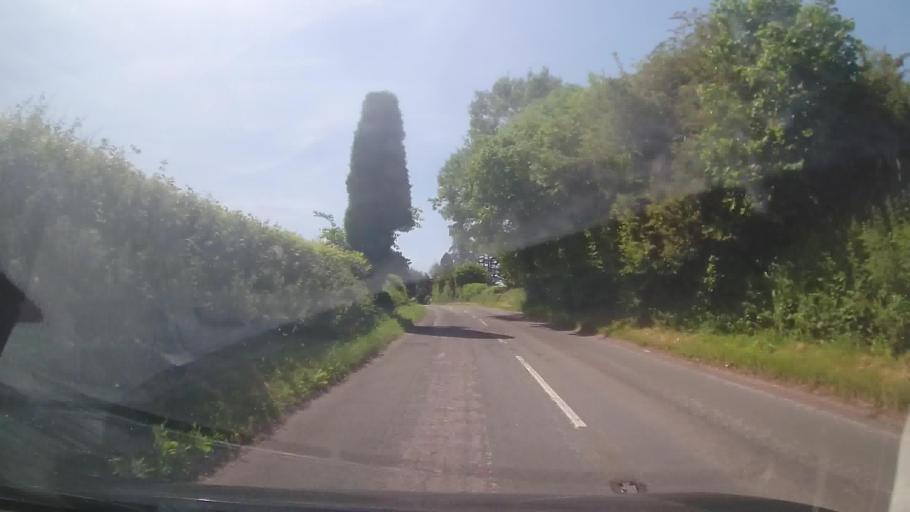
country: GB
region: England
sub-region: Herefordshire
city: Much Birch
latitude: 51.9700
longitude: -2.7404
